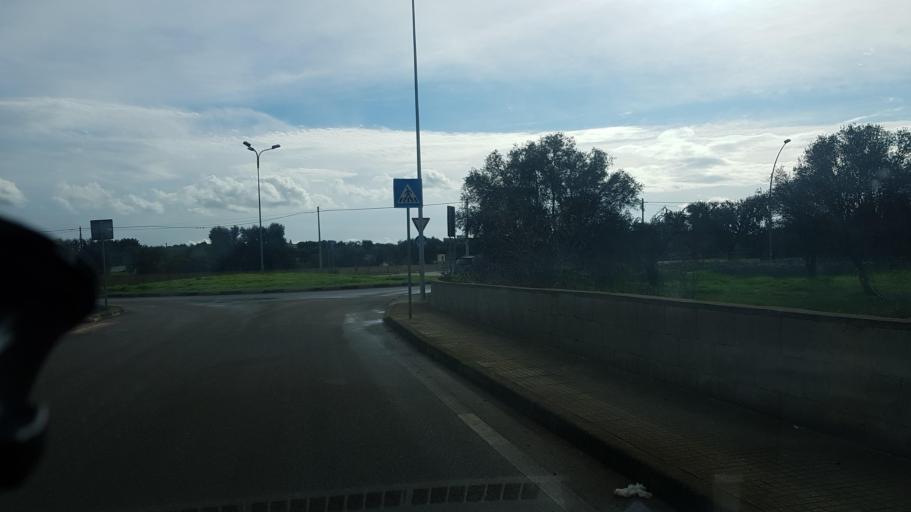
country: IT
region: Apulia
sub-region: Provincia di Brindisi
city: San Vito dei Normanni
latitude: 40.6615
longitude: 17.7159
